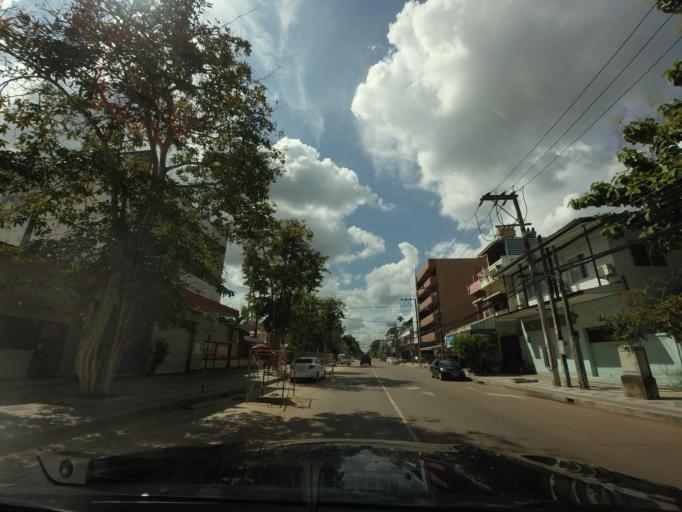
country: TH
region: Changwat Udon Thani
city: Udon Thani
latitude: 17.4052
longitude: 102.7863
